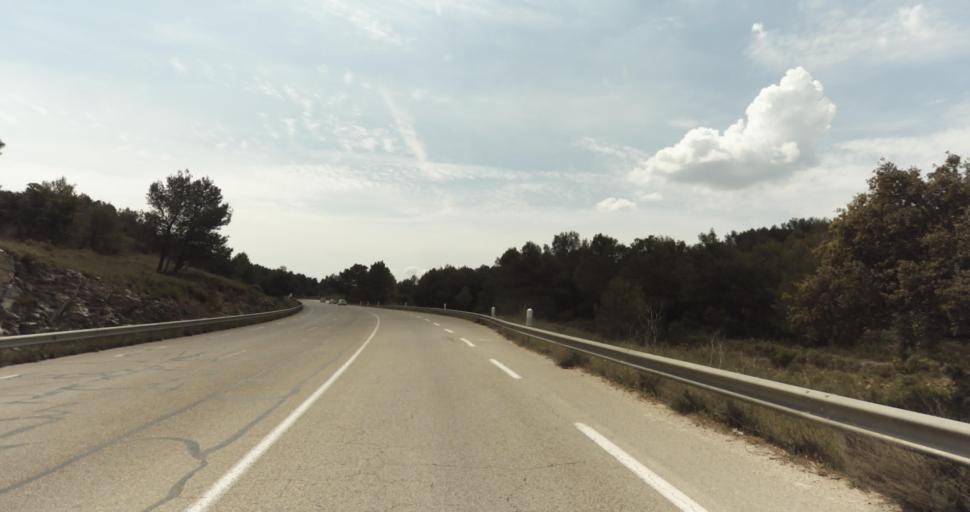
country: FR
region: Languedoc-Roussillon
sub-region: Departement du Gard
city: La Calmette
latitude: 43.8966
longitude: 4.2887
